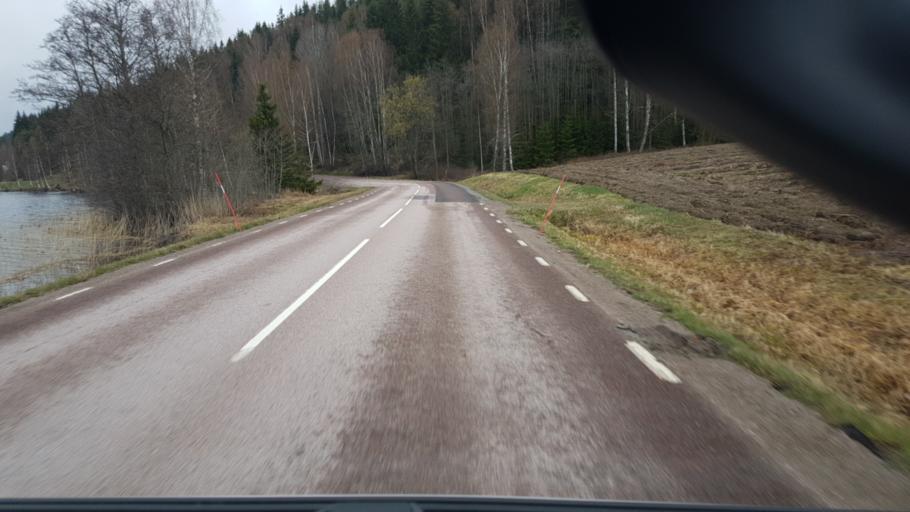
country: SE
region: Vaermland
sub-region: Arvika Kommun
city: Arvika
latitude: 59.8347
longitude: 12.5634
